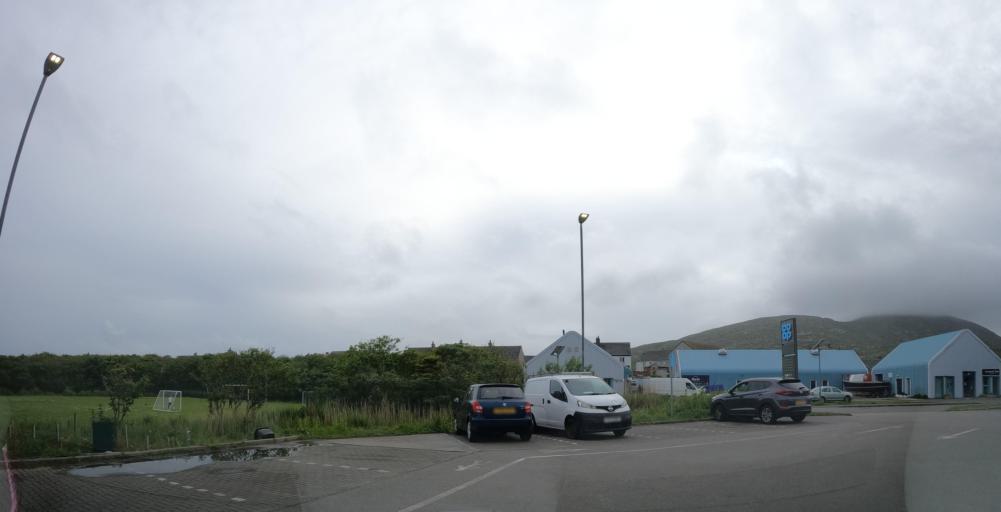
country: GB
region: Scotland
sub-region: Eilean Siar
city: Barra
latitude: 56.9552
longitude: -7.4982
